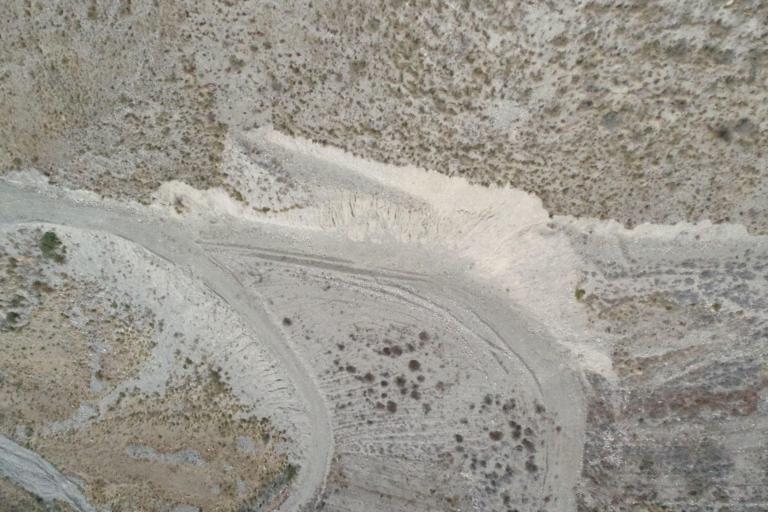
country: BO
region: La Paz
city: La Paz
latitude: -16.4735
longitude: -68.0979
